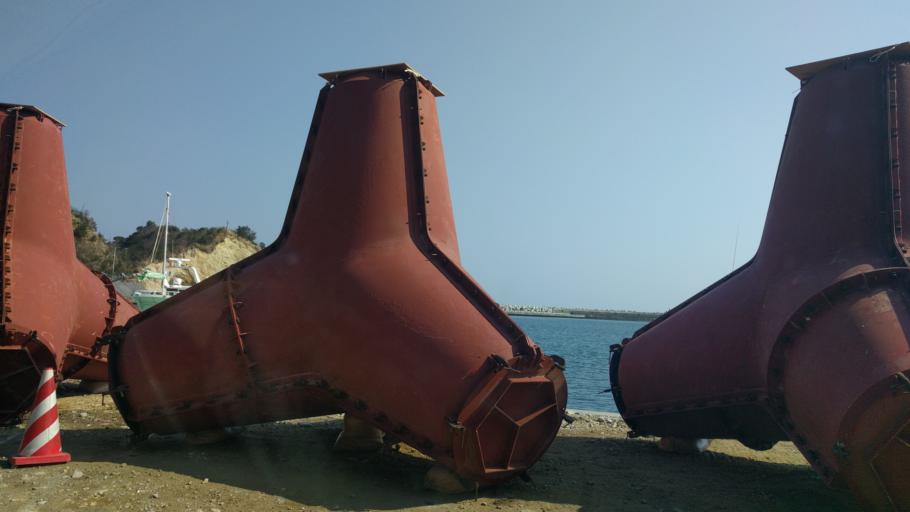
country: JP
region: Fukushima
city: Iwaki
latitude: 37.1494
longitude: 140.9998
